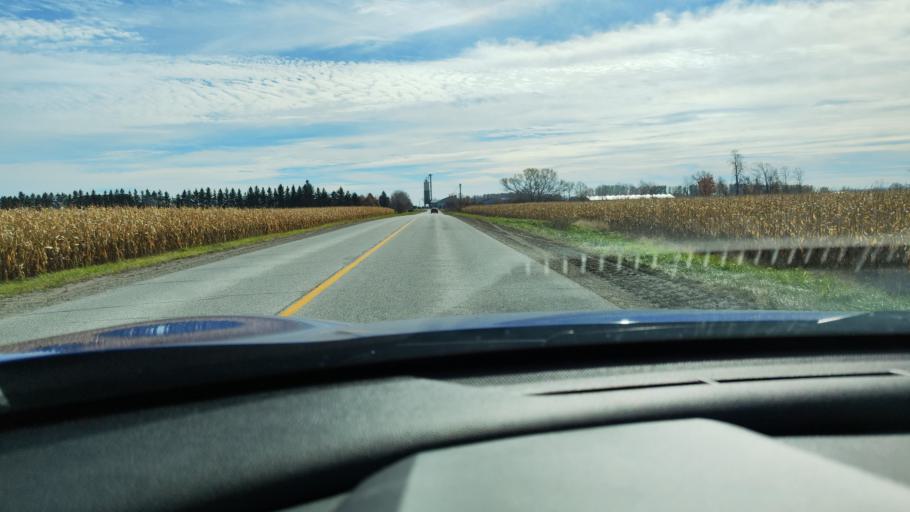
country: CA
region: Ontario
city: Wasaga Beach
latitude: 44.4447
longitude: -79.9997
